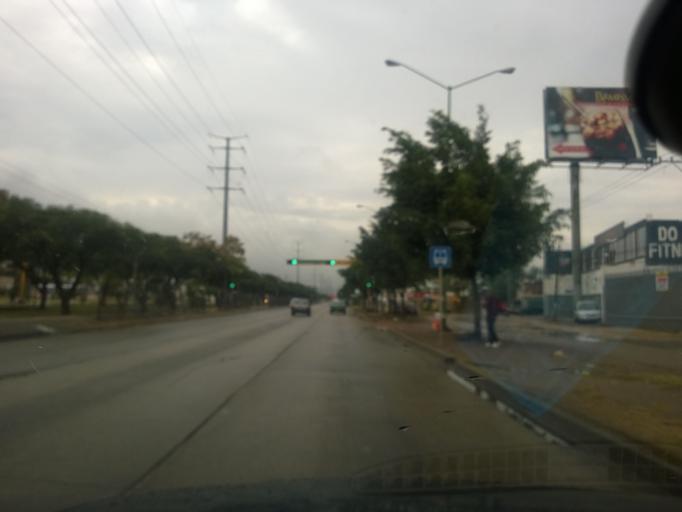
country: MX
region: Guanajuato
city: Leon
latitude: 21.1455
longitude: -101.6489
